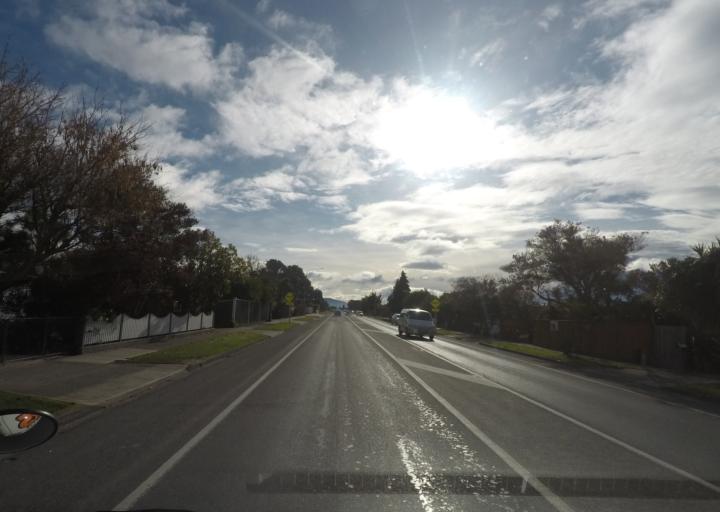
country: NZ
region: Tasman
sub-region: Tasman District
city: Motueka
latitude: -41.1284
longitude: 173.0102
